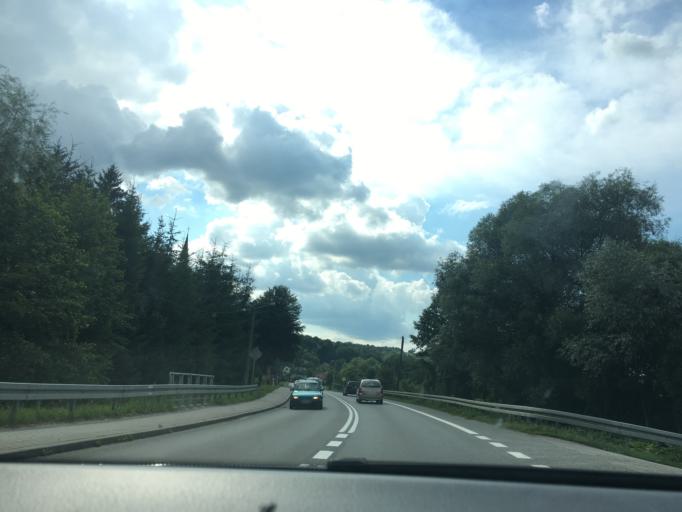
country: PL
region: Subcarpathian Voivodeship
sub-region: Powiat strzyzowski
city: Polomia
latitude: 49.8991
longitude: 21.8790
